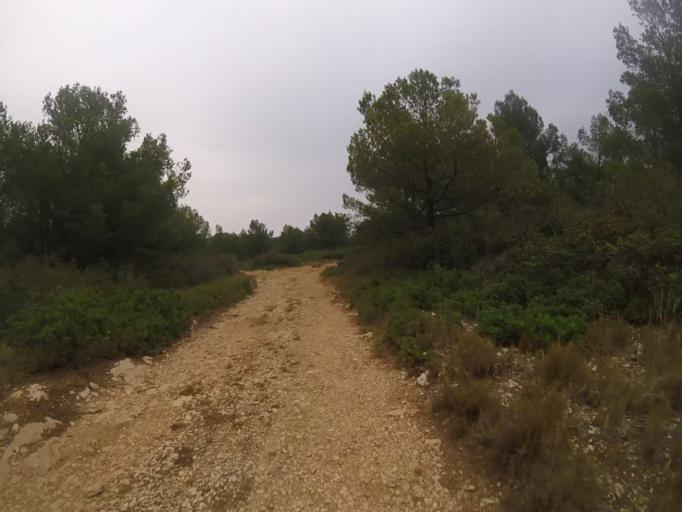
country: ES
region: Valencia
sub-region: Provincia de Castello
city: Alcoceber
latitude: 40.2853
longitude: 0.2851
